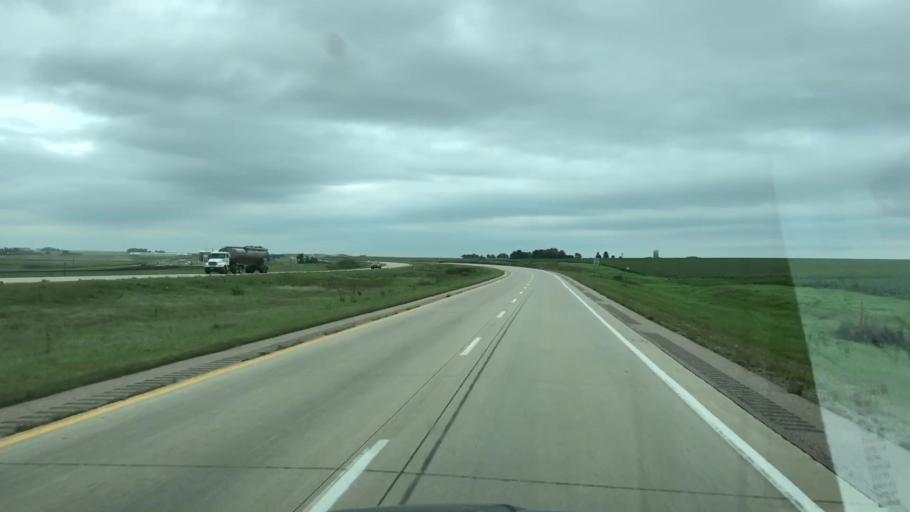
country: US
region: Iowa
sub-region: O'Brien County
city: Sheldon
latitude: 43.0893
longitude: -95.8982
